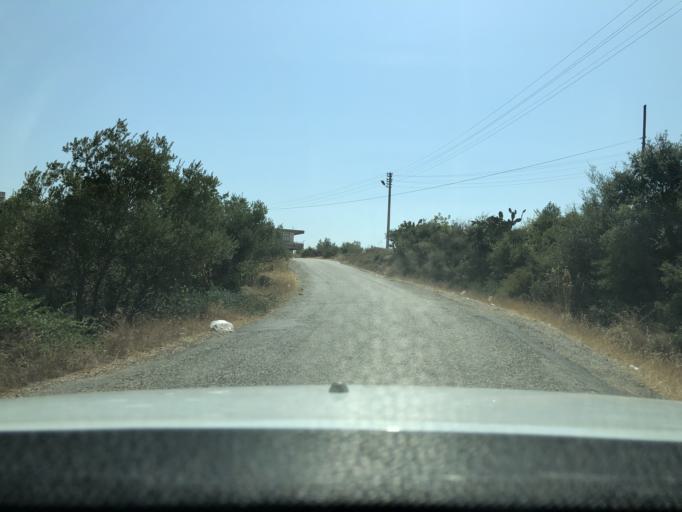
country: TR
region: Antalya
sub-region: Manavgat
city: Manavgat
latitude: 36.8044
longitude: 31.4718
